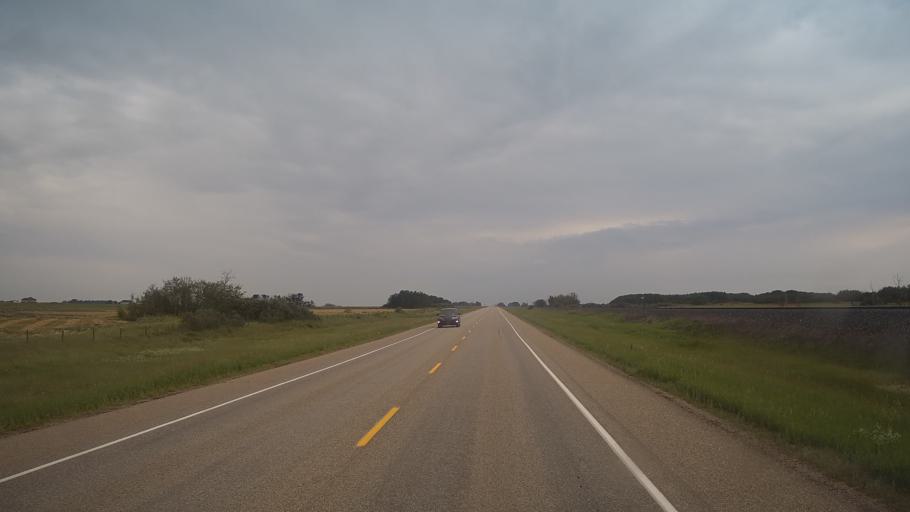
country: CA
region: Saskatchewan
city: Langham
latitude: 52.1269
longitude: -107.2688
